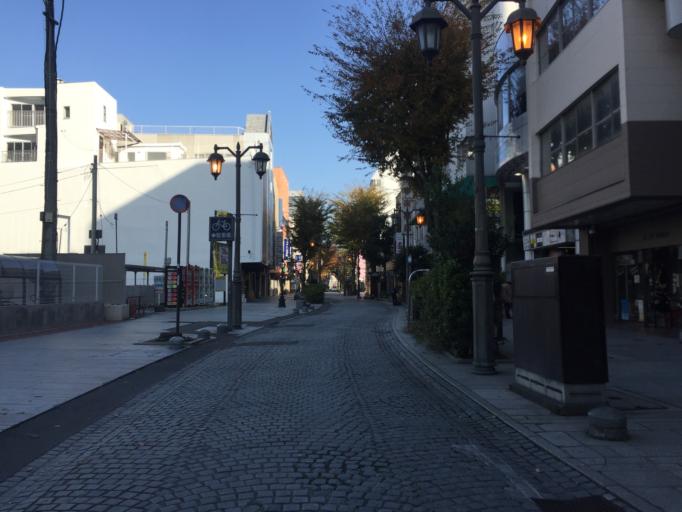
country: JP
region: Fukushima
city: Fukushima-shi
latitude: 37.7544
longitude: 140.4648
